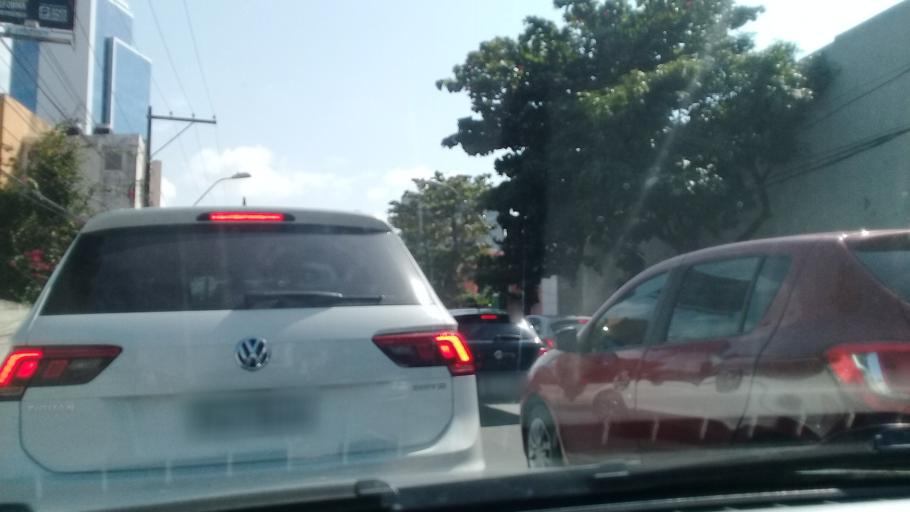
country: BR
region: Pernambuco
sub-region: Recife
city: Recife
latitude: -8.0912
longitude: -34.8837
